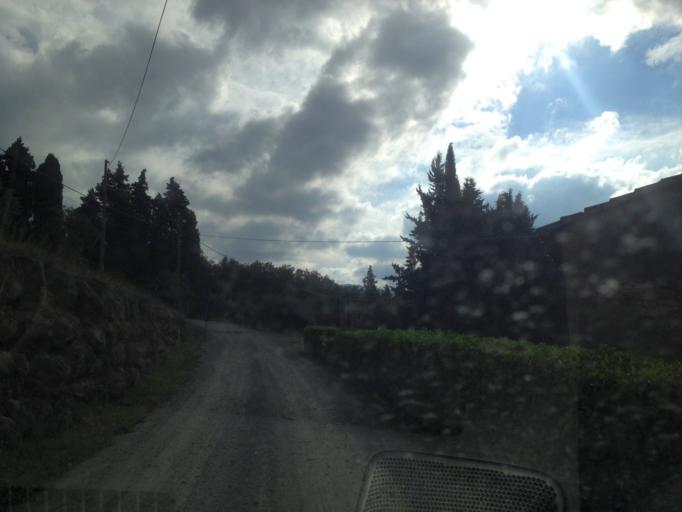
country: IT
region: Tuscany
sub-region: Province of Florence
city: Dicomano
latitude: 43.8606
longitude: 11.5061
